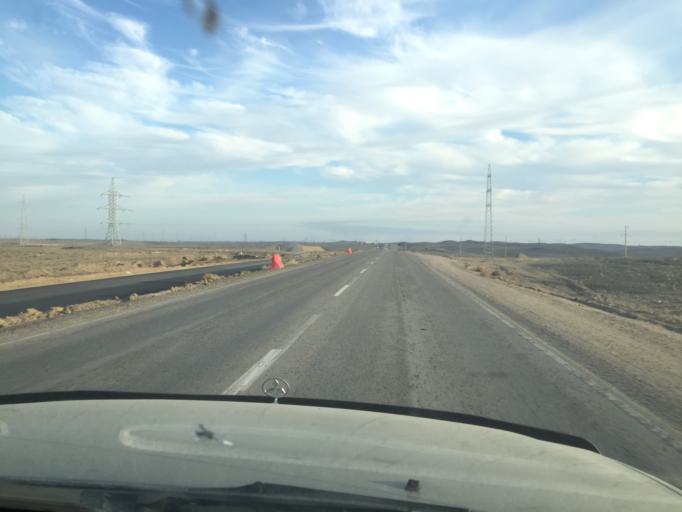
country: KZ
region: Almaty Oblysy
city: Ulken
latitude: 45.2137
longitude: 73.8715
